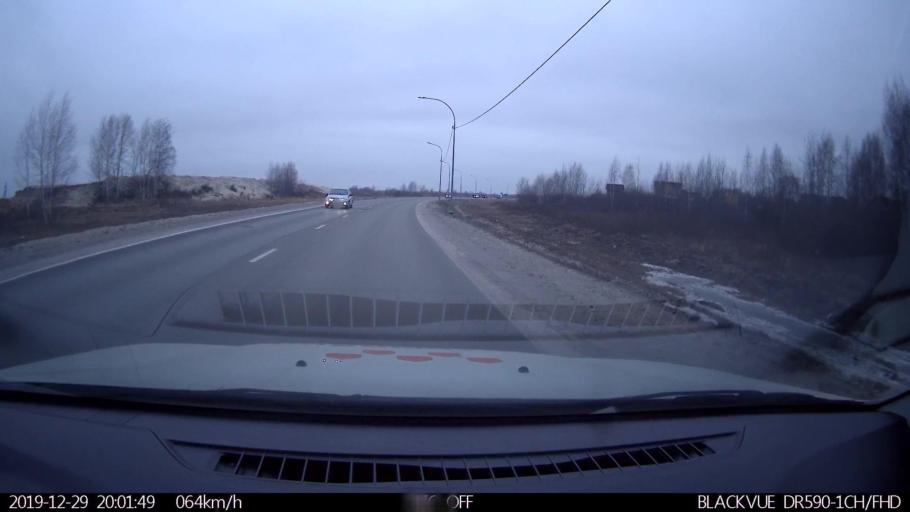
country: RU
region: Nizjnij Novgorod
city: Bor
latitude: 56.3607
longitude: 44.0376
